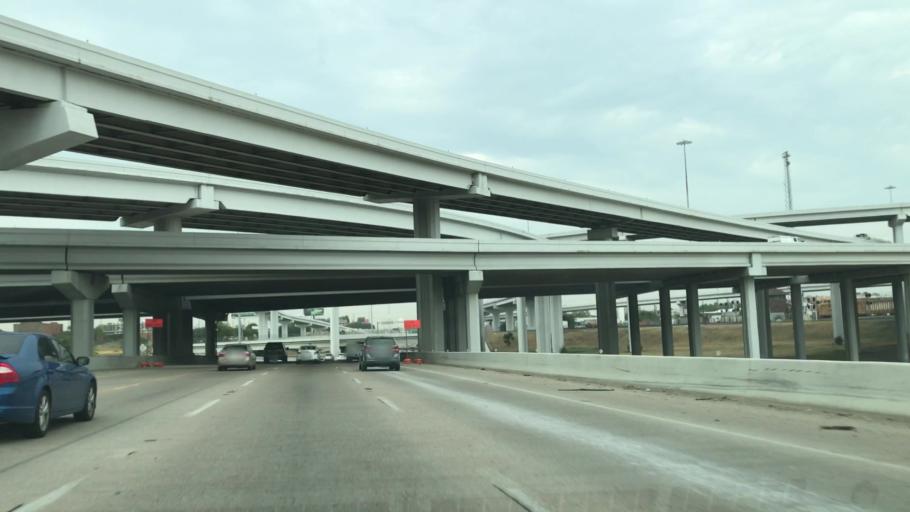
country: US
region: Texas
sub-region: Tarrant County
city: Fort Worth
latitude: 32.7474
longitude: -97.3197
